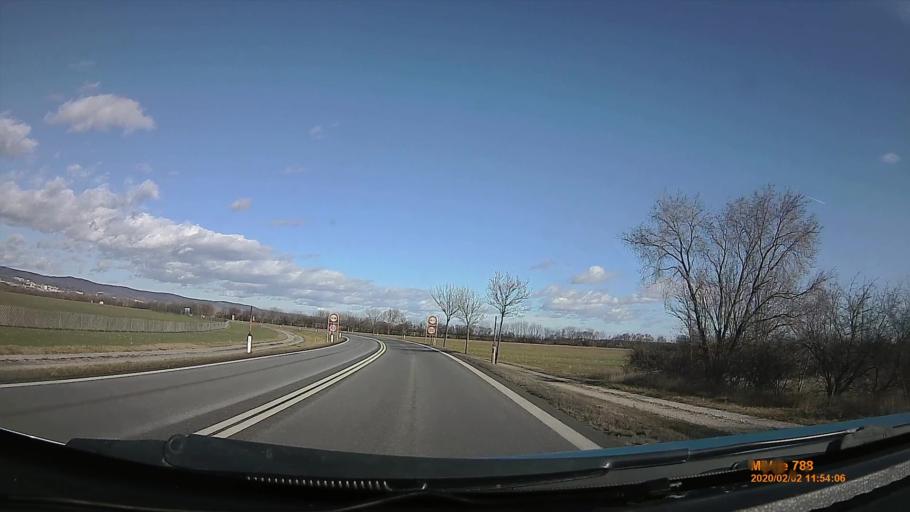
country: AT
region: Burgenland
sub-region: Eisenstadt-Umgebung
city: Wulkaprodersdorf
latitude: 47.7909
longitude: 16.5176
